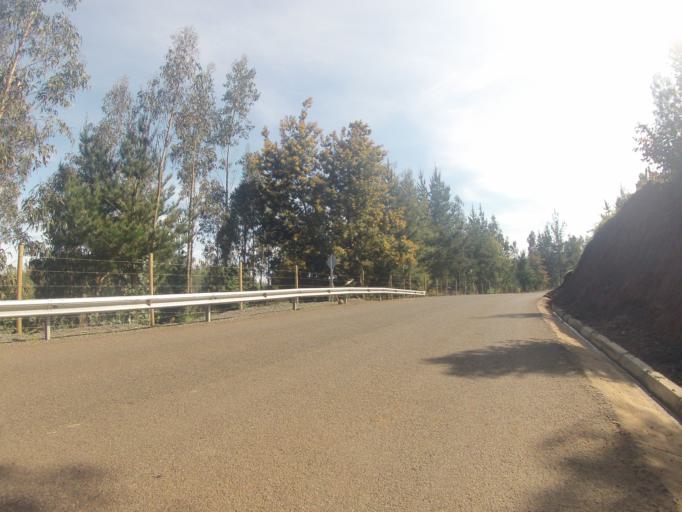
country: CL
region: Araucania
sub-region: Provincia de Cautin
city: Temuco
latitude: -38.7029
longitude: -72.5943
